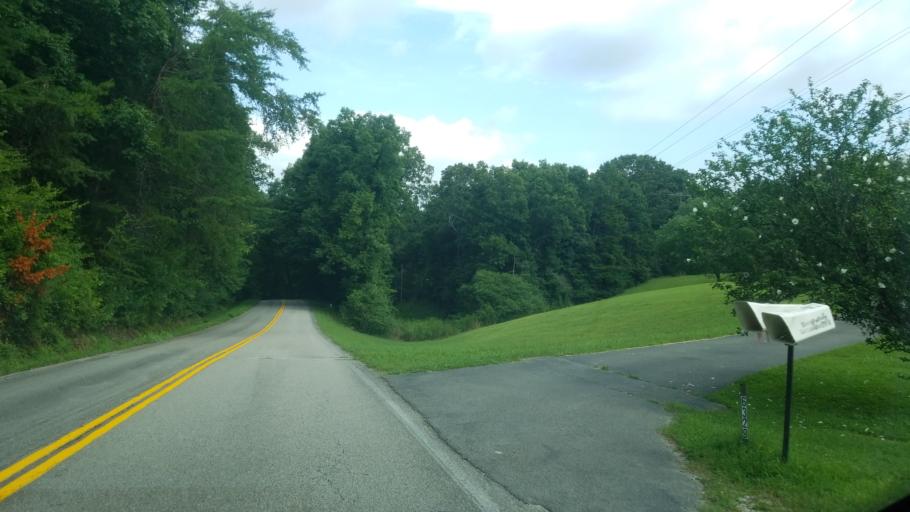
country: US
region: Tennessee
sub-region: Hamilton County
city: Lakesite
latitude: 35.1822
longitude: -85.0967
